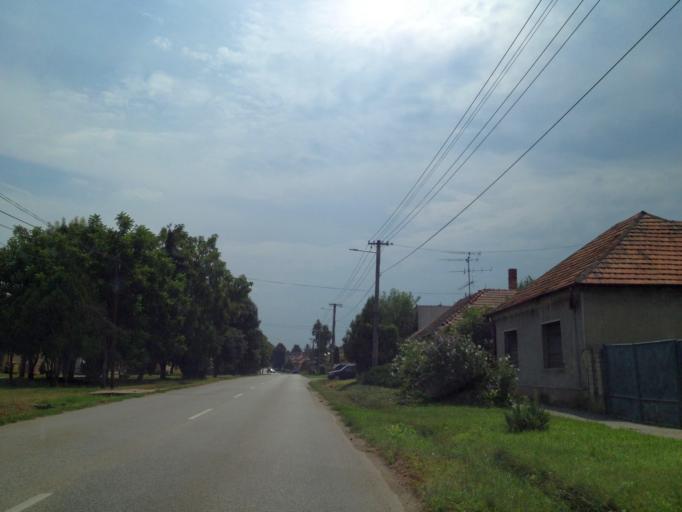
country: SK
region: Nitriansky
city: Svodin
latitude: 47.8494
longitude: 18.5125
